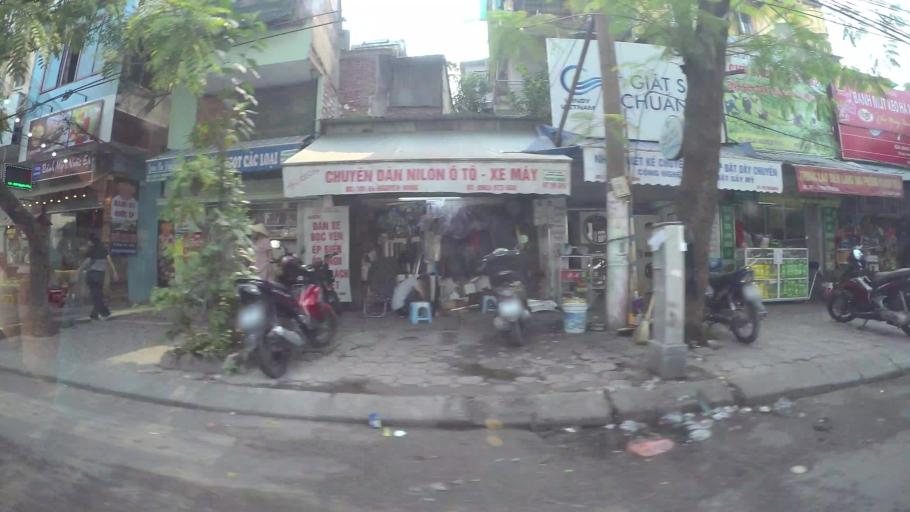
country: VN
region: Ha Noi
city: Cau Giay
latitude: 21.0224
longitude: 105.8120
